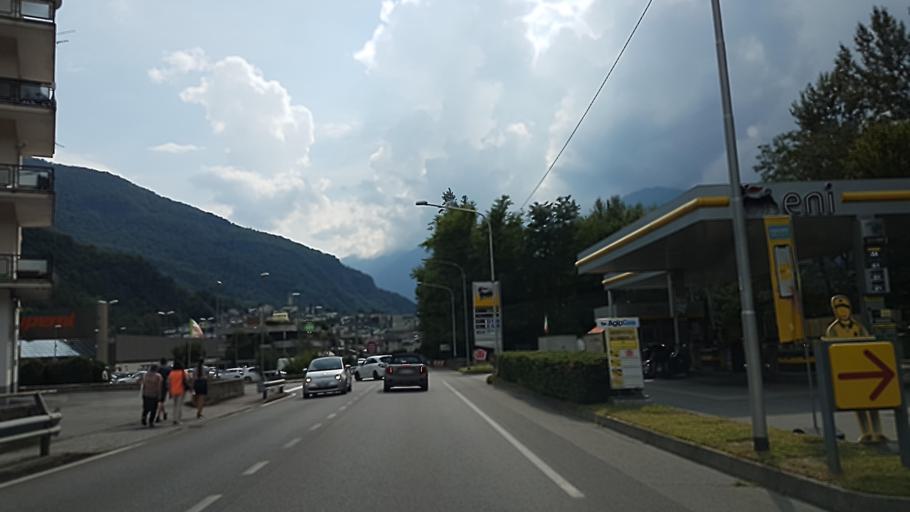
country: IT
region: Lombardy
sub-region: Provincia di Sondrio
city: Prata Centro
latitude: 46.3133
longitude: 9.3973
